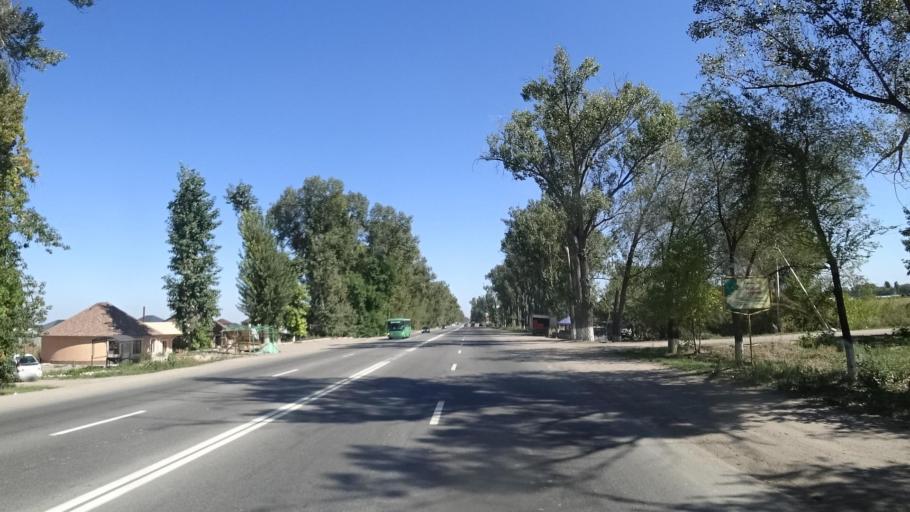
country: KZ
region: Almaty Oblysy
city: Energeticheskiy
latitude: 43.3571
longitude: 77.0726
